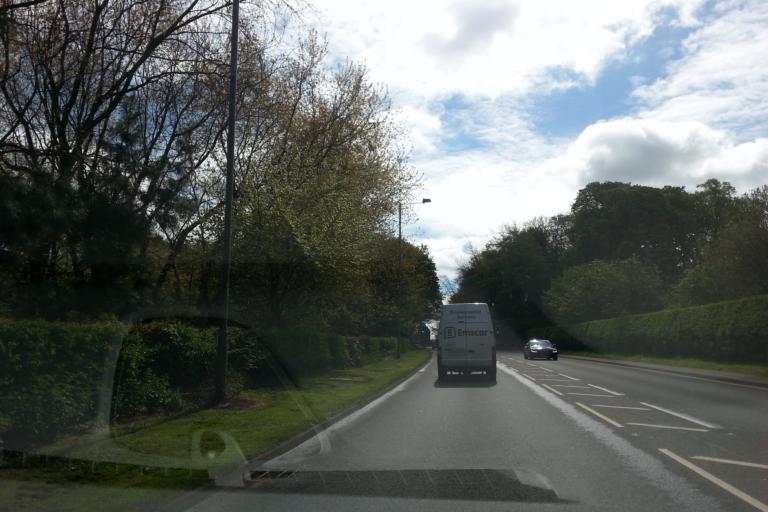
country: GB
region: England
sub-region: Staffordshire
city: Lichfield
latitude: 52.6827
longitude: -1.8411
